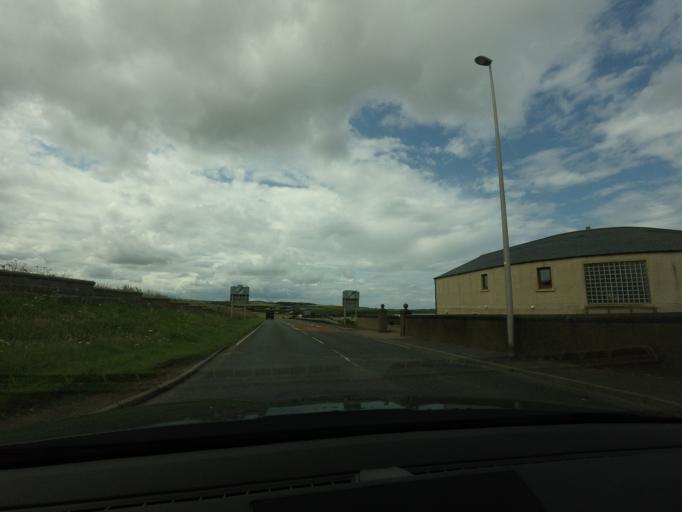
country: GB
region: Scotland
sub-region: Aberdeenshire
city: Banff
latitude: 57.6680
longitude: -2.5402
